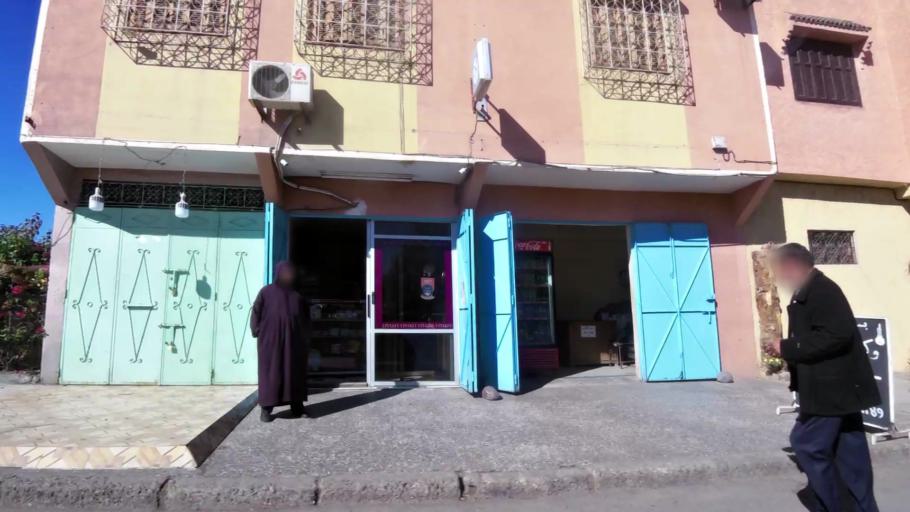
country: MA
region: Marrakech-Tensift-Al Haouz
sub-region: Marrakech
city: Marrakesh
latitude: 31.5912
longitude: -8.0344
